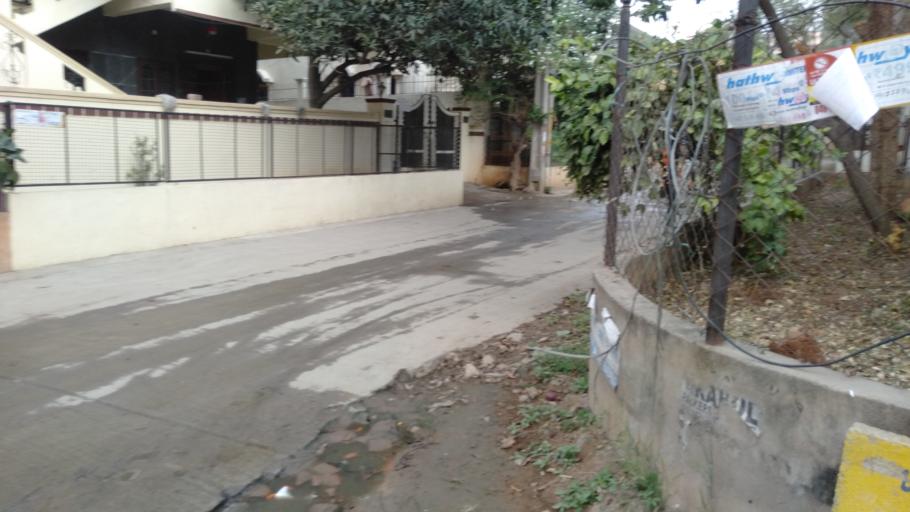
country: IN
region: Telangana
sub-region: Rangareddi
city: Kukatpalli
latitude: 17.4918
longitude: 78.3875
